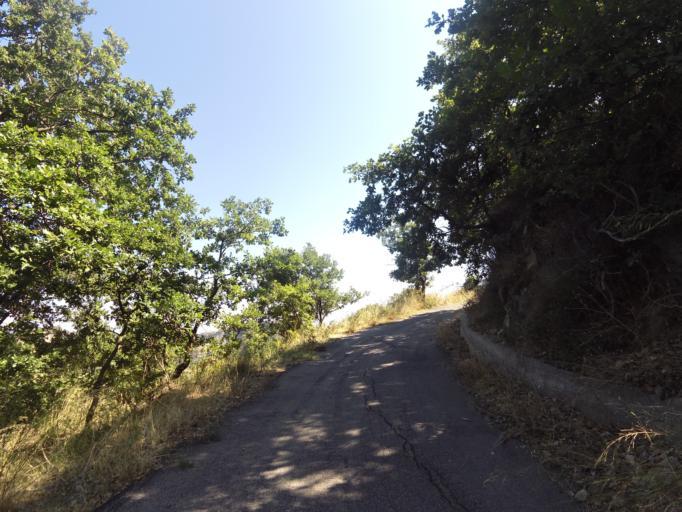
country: IT
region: Calabria
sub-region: Provincia di Reggio Calabria
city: Pazzano
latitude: 38.4591
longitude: 16.4593
